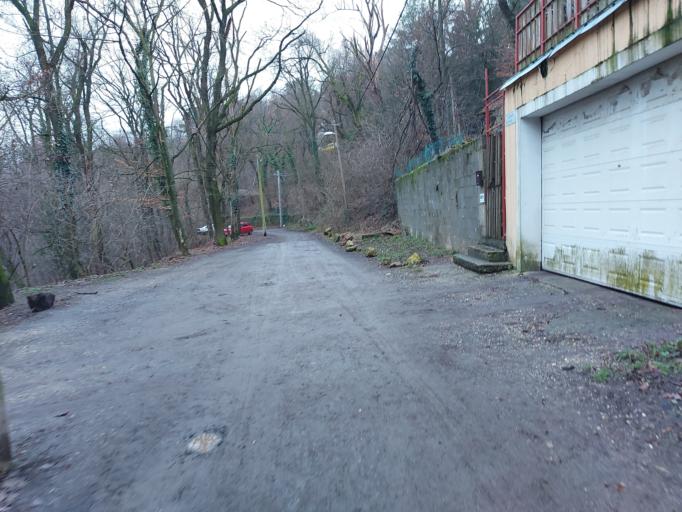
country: HU
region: Pest
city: Budaors
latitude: 47.4890
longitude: 18.9703
